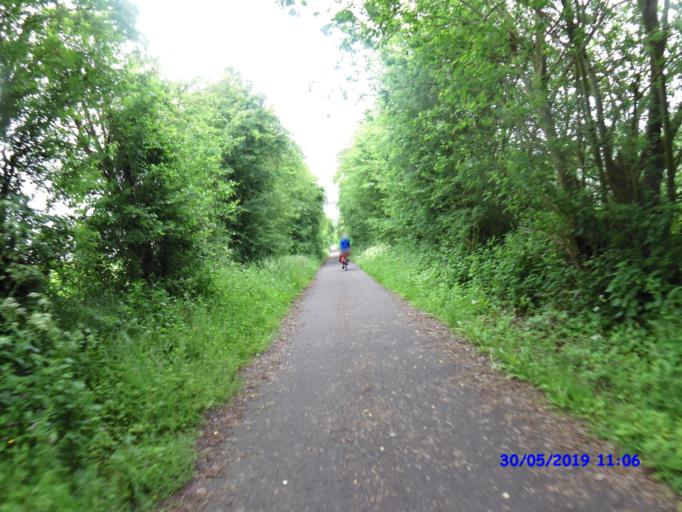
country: BE
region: Wallonia
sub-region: Province du Hainaut
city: Thuin
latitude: 50.2855
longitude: 4.3246
